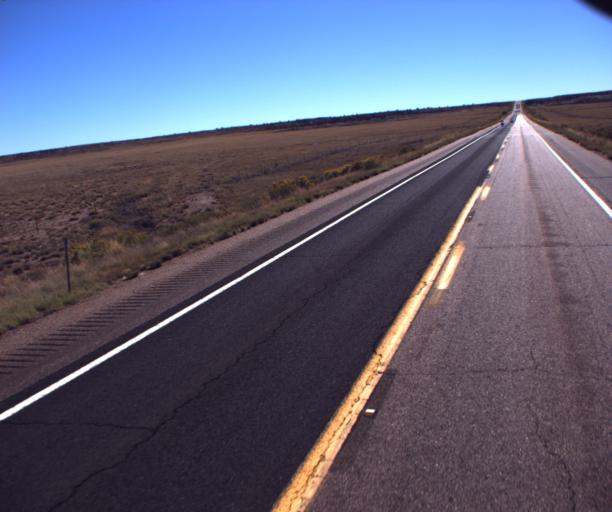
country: US
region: Arizona
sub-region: Navajo County
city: Snowflake
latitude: 34.7266
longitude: -109.7784
